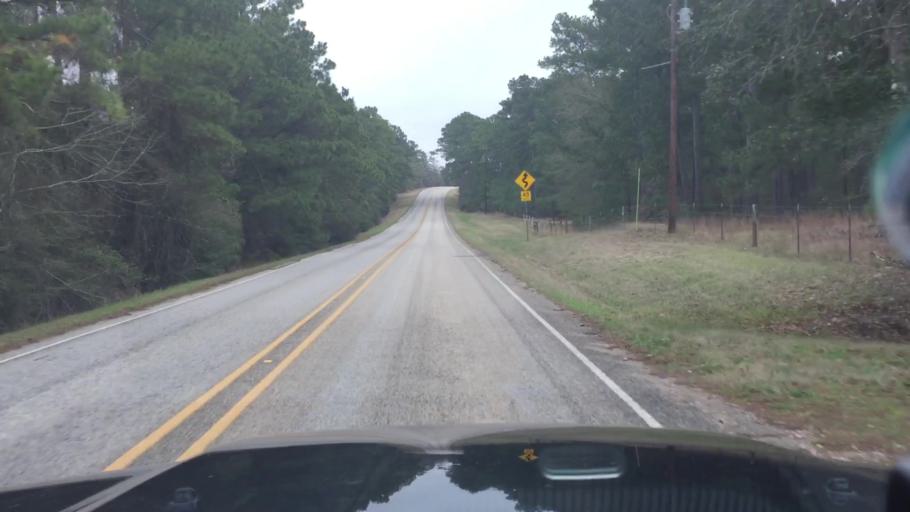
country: US
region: Texas
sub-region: Fayette County
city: La Grange
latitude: 30.0118
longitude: -96.9359
